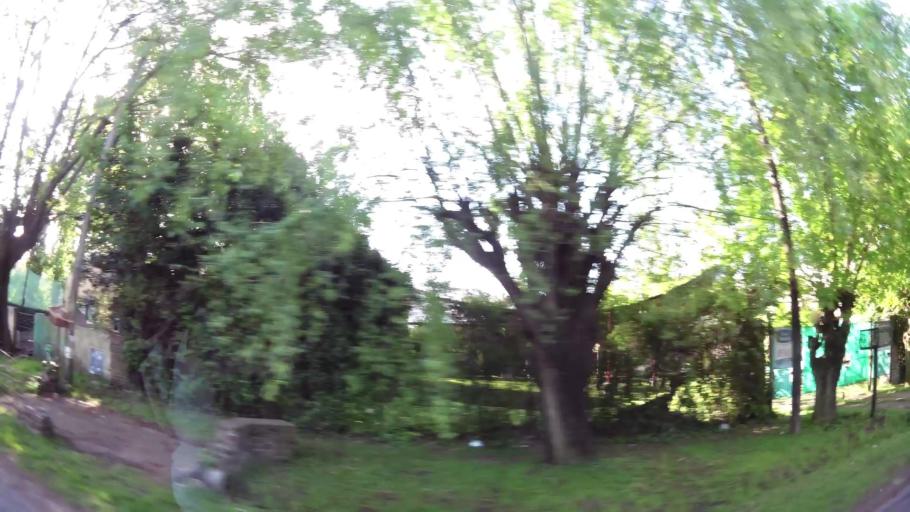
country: AR
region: Buenos Aires
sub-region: Partido de Quilmes
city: Quilmes
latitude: -34.8129
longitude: -58.2133
